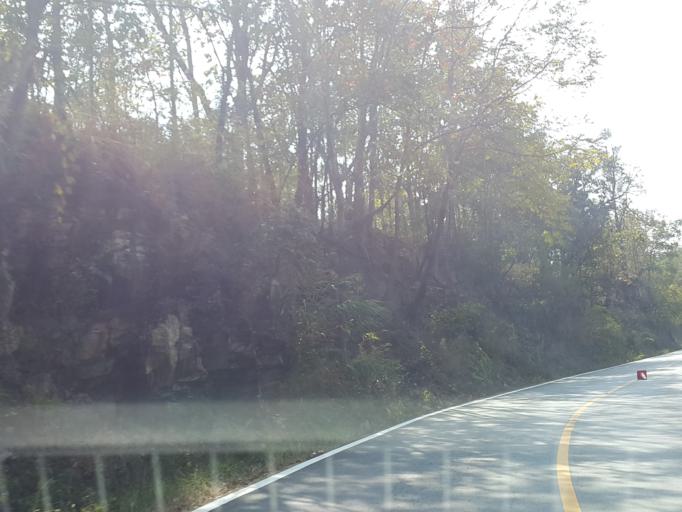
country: TH
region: Chiang Mai
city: Hot
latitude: 18.1806
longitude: 98.4526
